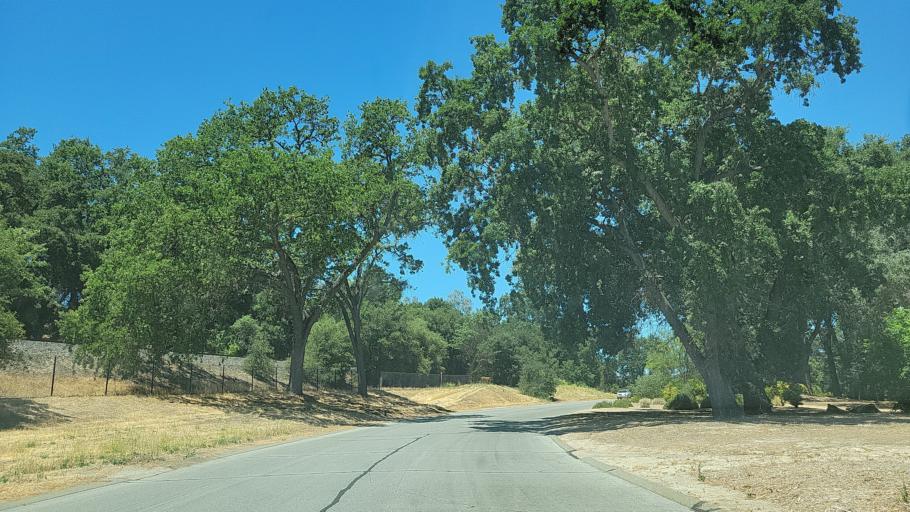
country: US
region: California
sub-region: San Luis Obispo County
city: Atascadero
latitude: 35.5120
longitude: -120.6720
